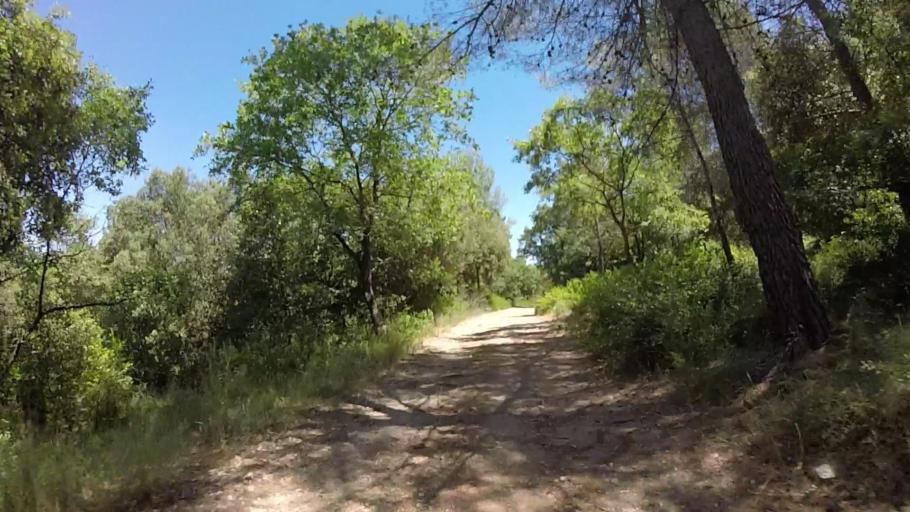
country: FR
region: Provence-Alpes-Cote d'Azur
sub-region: Departement des Alpes-Maritimes
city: Valbonne
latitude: 43.6302
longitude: 7.0470
